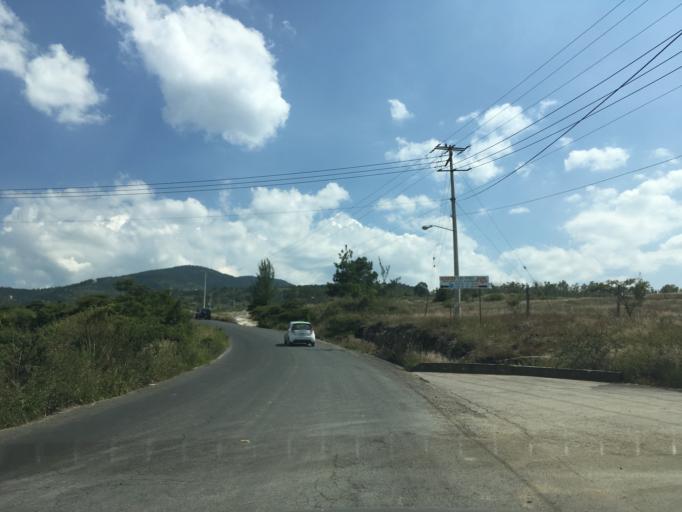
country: MX
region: Michoacan
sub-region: Morelia
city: Morelos
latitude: 19.6514
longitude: -101.2027
